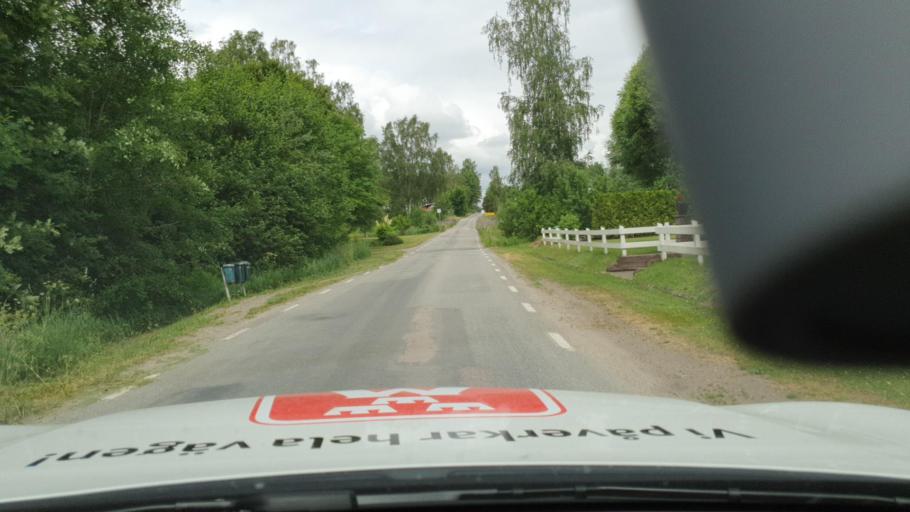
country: SE
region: Vaestra Goetaland
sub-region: Tidaholms Kommun
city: Tidaholm
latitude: 58.1476
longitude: 14.0259
